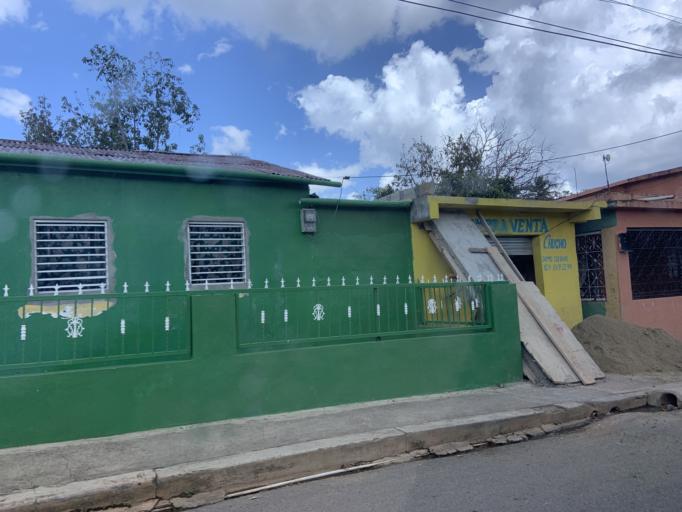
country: DO
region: Monte Plata
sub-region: Yamasa
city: Yamasa
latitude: 18.7760
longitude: -70.0286
